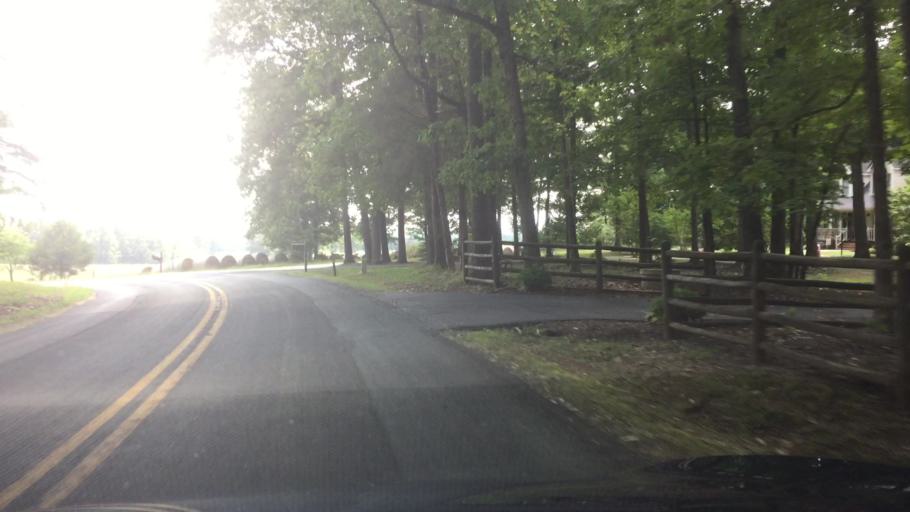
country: US
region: Virginia
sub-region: Appomattox County
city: Appomattox
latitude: 37.3365
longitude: -78.8811
